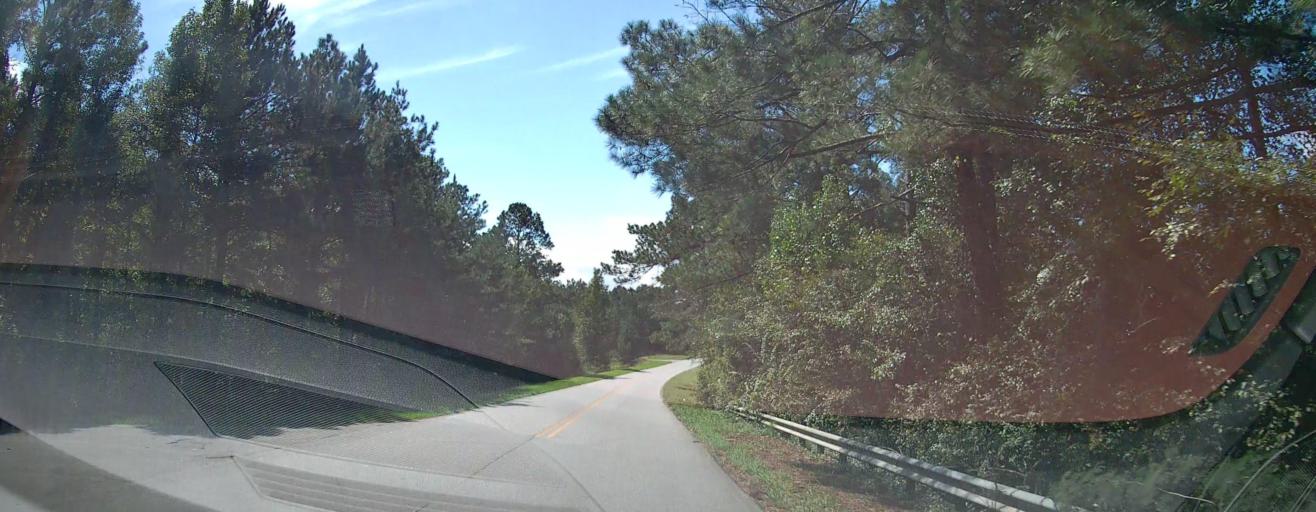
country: US
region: Georgia
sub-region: Houston County
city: Warner Robins
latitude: 32.7177
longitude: -83.5340
